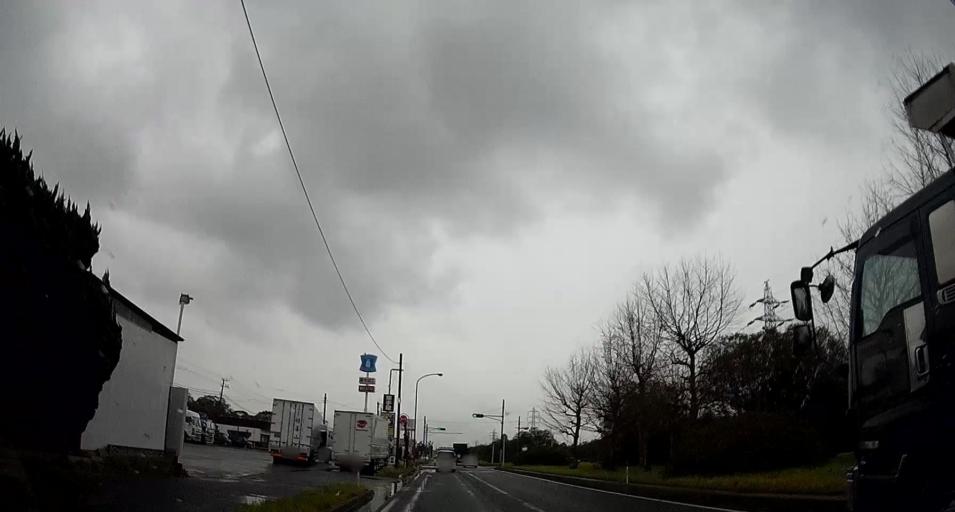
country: JP
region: Chiba
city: Ichihara
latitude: 35.5270
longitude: 140.0663
